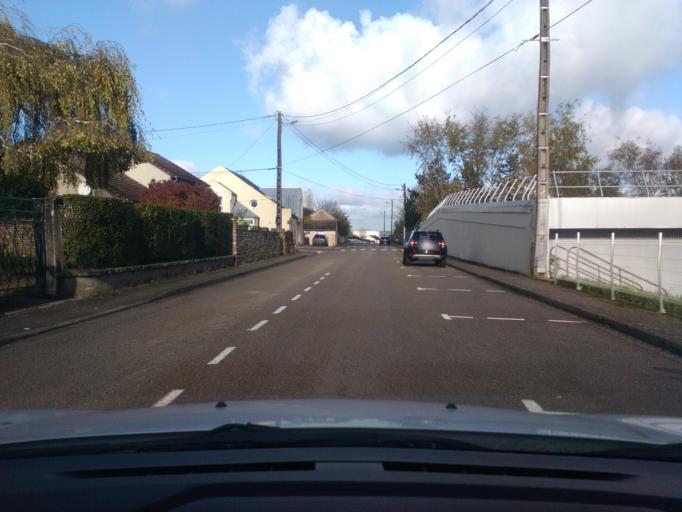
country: FR
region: Lorraine
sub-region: Departement des Vosges
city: Mirecourt
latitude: 48.3040
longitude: 6.1312
